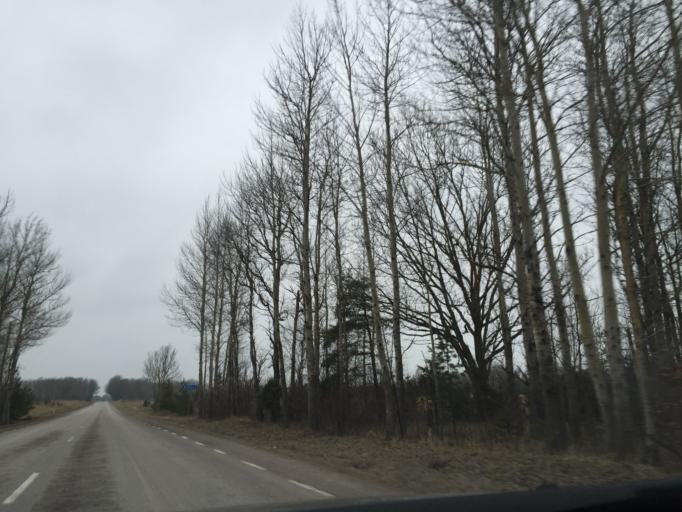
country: EE
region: Saare
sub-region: Kuressaare linn
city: Kuressaare
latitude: 58.2892
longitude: 22.2991
